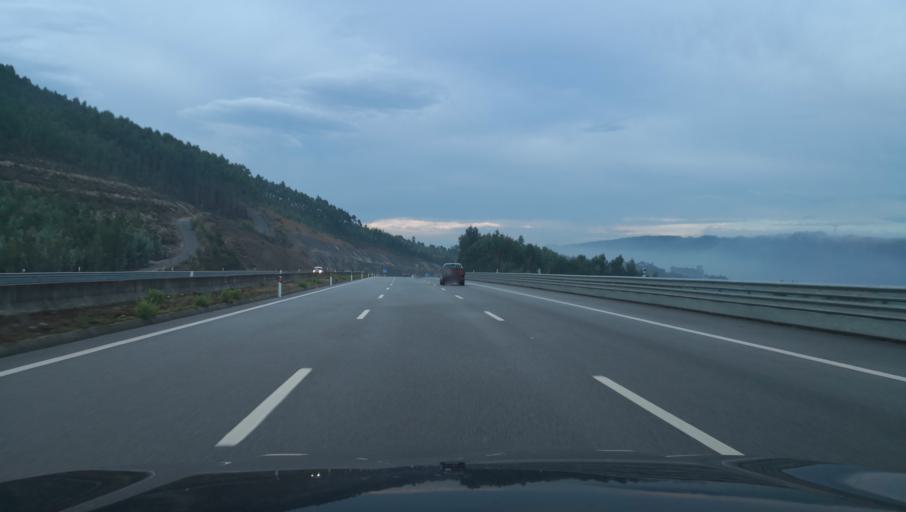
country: PT
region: Porto
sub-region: Paredes
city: Recarei
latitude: 41.1166
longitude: -8.4329
